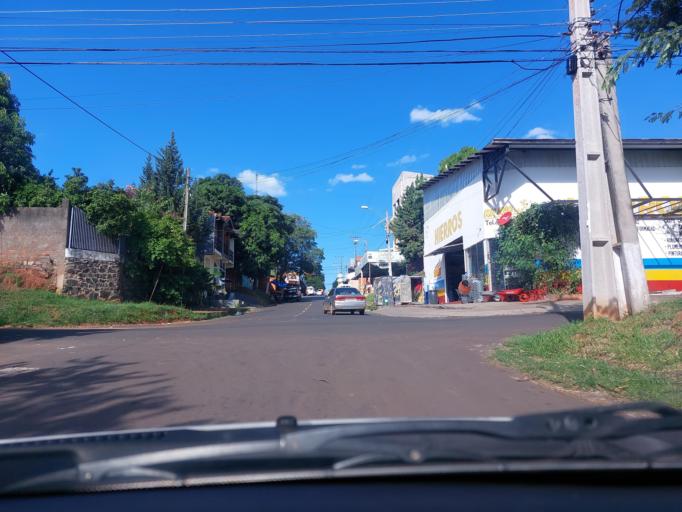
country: PY
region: San Pedro
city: Guayaybi
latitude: -24.6636
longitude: -56.4461
